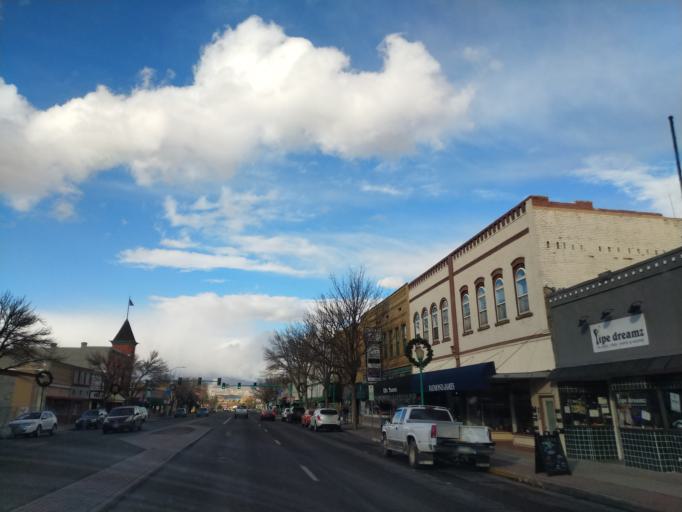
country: US
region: Colorado
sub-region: Delta County
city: Delta
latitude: 38.7419
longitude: -108.0708
